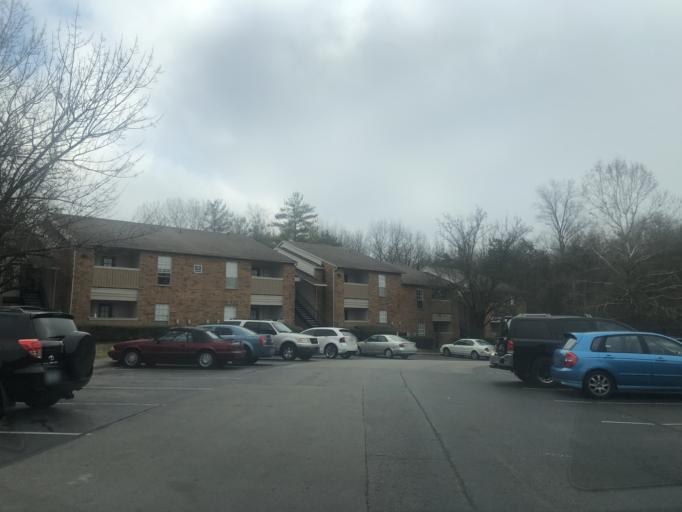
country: US
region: Tennessee
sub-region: Rutherford County
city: La Vergne
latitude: 36.0644
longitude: -86.6422
